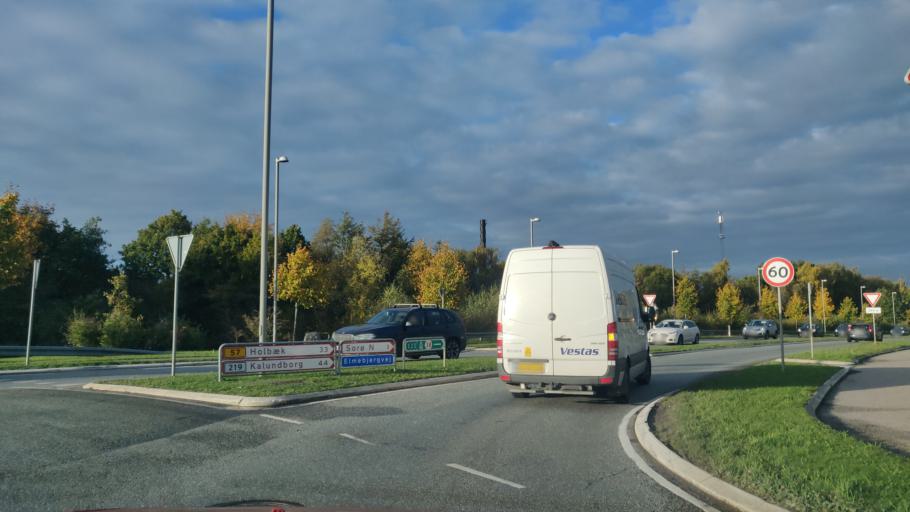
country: DK
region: Zealand
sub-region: Soro Kommune
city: Soro
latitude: 55.4610
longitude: 11.5636
